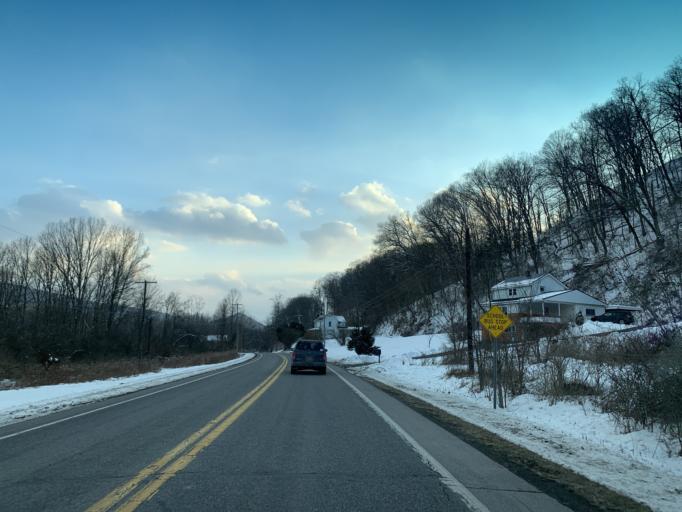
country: US
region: Maryland
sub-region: Allegany County
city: Cumberland
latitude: 39.7417
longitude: -78.7588
